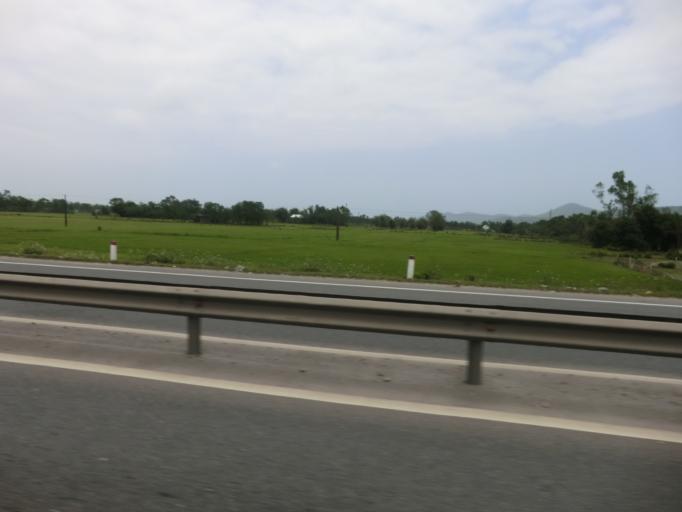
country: VN
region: Thua Thien-Hue
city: Phu Loc
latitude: 16.2702
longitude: 108.0184
